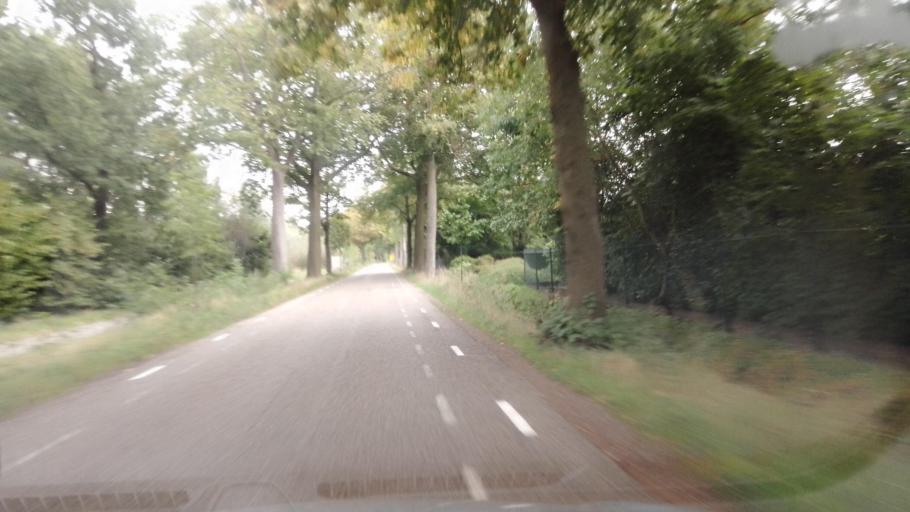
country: NL
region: Limburg
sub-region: Gemeente Peel en Maas
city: Maasbree
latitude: 51.4197
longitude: 6.0747
